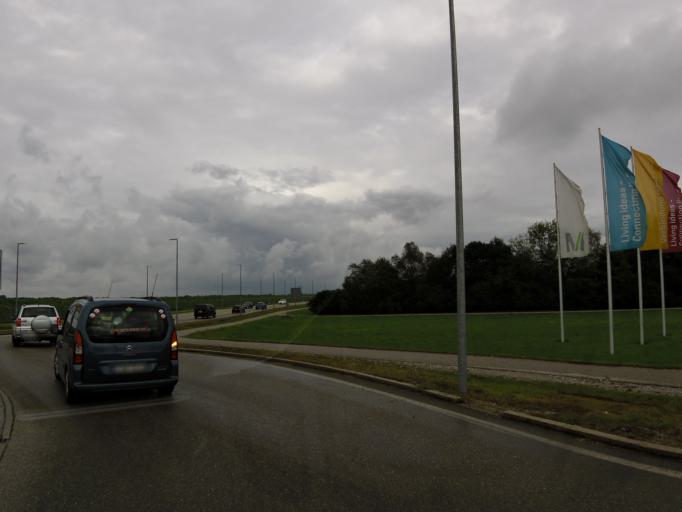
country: DE
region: Bavaria
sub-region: Upper Bavaria
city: Marzling
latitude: 48.3606
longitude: 11.8059
